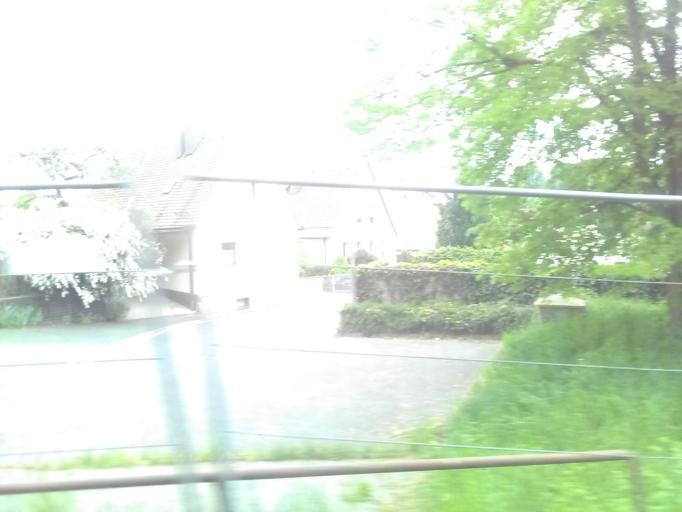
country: DE
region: Bavaria
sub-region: Regierungsbezirk Mittelfranken
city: Heroldsberg
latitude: 49.5313
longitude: 11.1493
